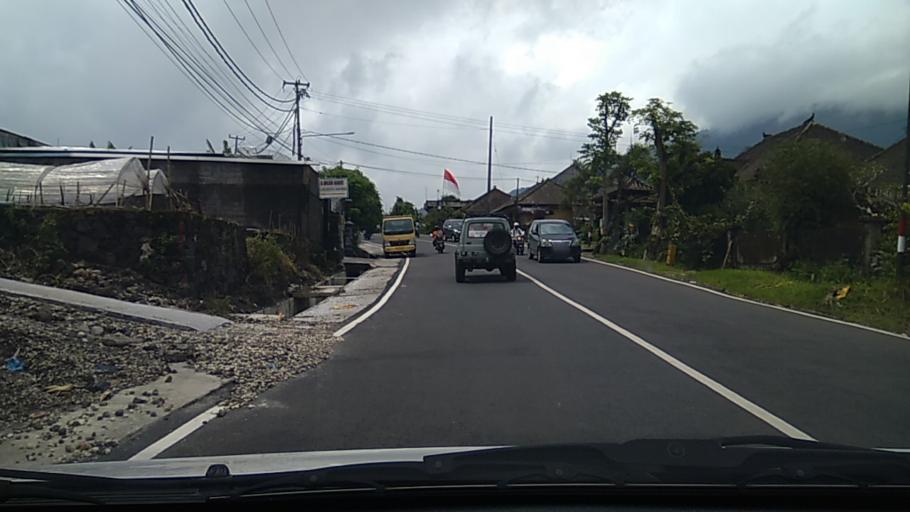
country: ID
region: Bali
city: Munduk
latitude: -8.2635
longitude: 115.1649
